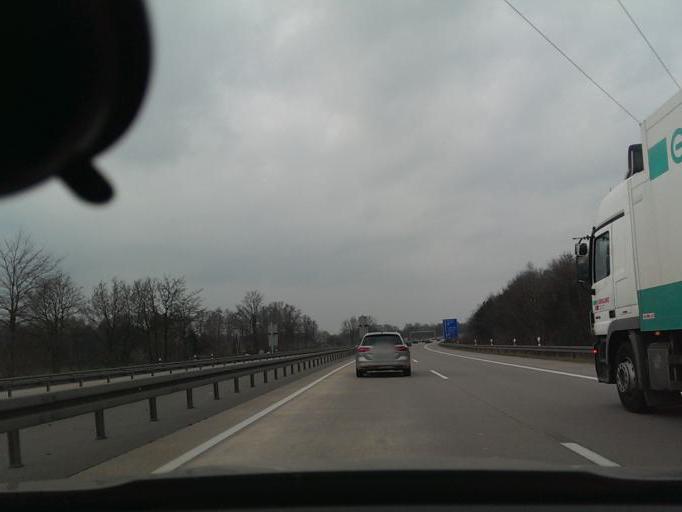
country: DE
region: Lower Saxony
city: Garbsen-Mitte
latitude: 52.4307
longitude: 9.6687
